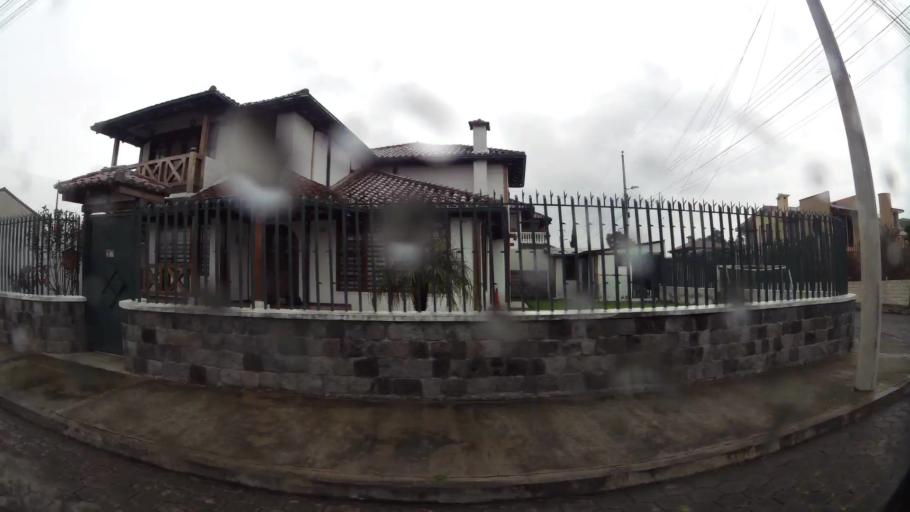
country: EC
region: Pichincha
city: Sangolqui
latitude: -0.3209
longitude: -78.4332
